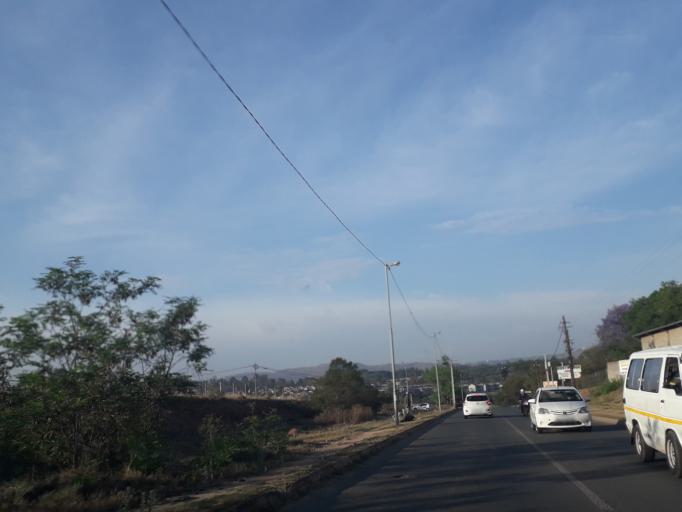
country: ZA
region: Gauteng
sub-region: West Rand District Municipality
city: Muldersdriseloop
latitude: -26.0801
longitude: 27.9072
